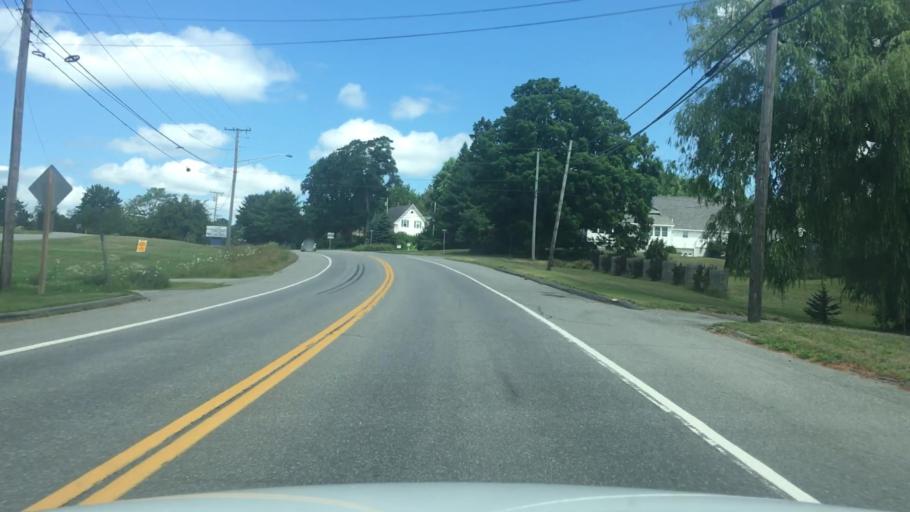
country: US
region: Maine
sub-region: Waldo County
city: Belfast
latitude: 44.3975
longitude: -68.9874
